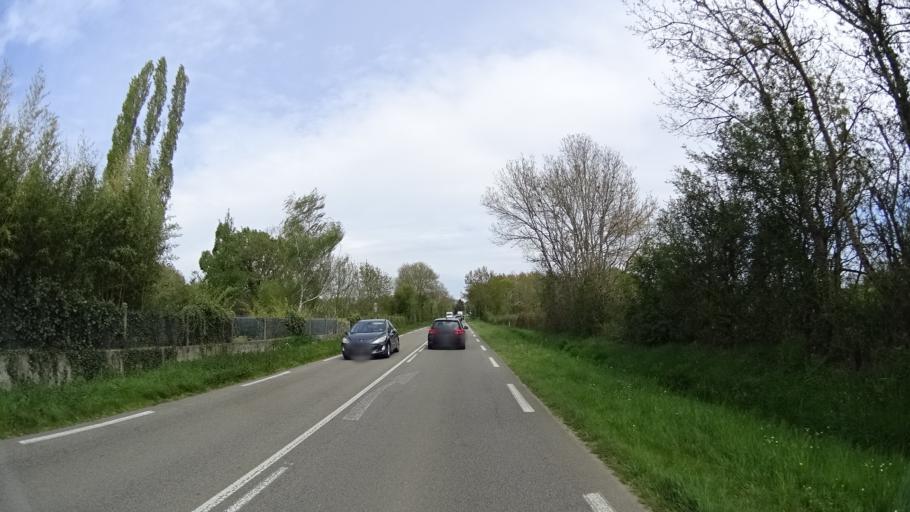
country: FR
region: Pays de la Loire
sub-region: Departement de la Loire-Atlantique
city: Port-Saint-Pere
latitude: 47.1238
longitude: -1.7637
